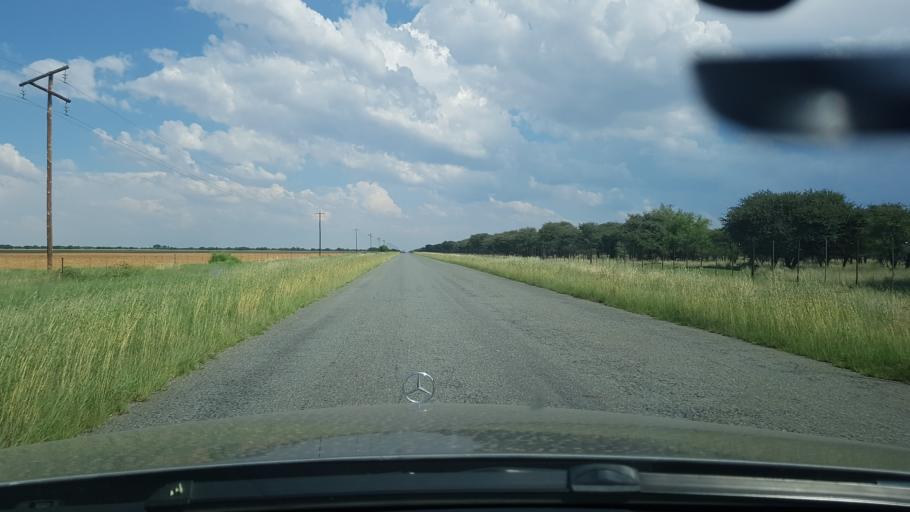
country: ZA
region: North-West
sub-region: Dr Ruth Segomotsi Mompati District Municipality
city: Bloemhof
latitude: -27.7474
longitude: 25.5905
